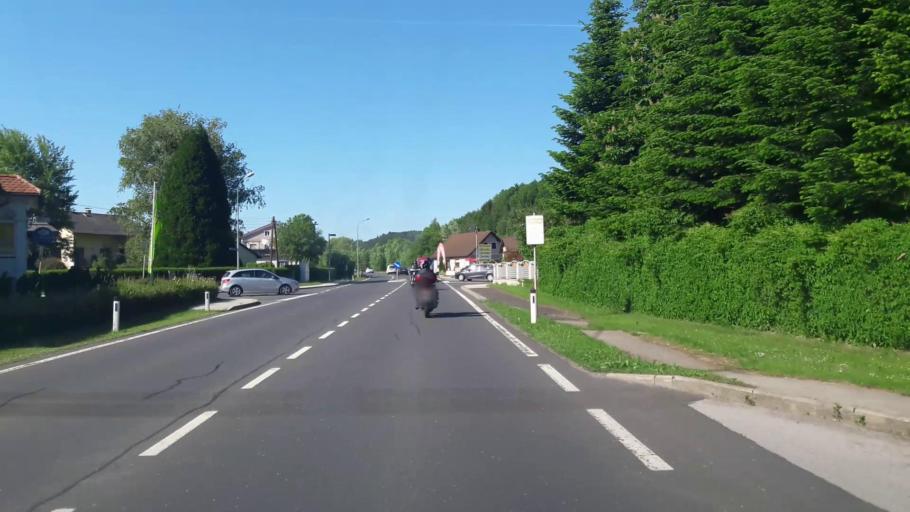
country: AT
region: Burgenland
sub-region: Politischer Bezirk Oberwart
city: Kemeten
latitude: 47.2491
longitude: 16.1526
